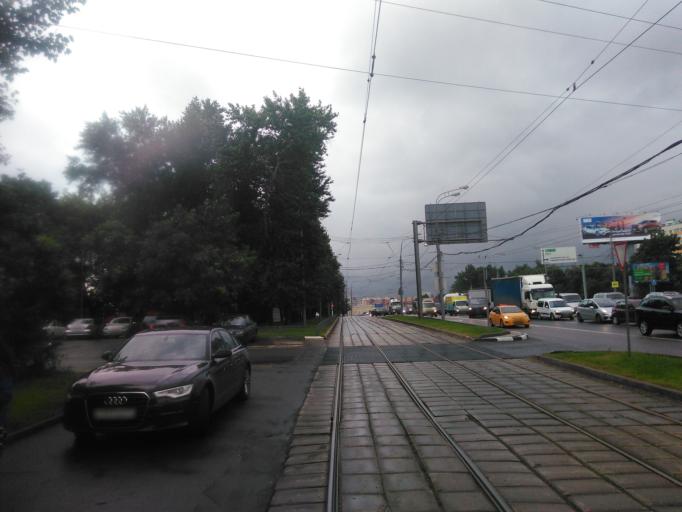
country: RU
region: Moscow
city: Nagornyy
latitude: 55.6689
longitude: 37.6251
